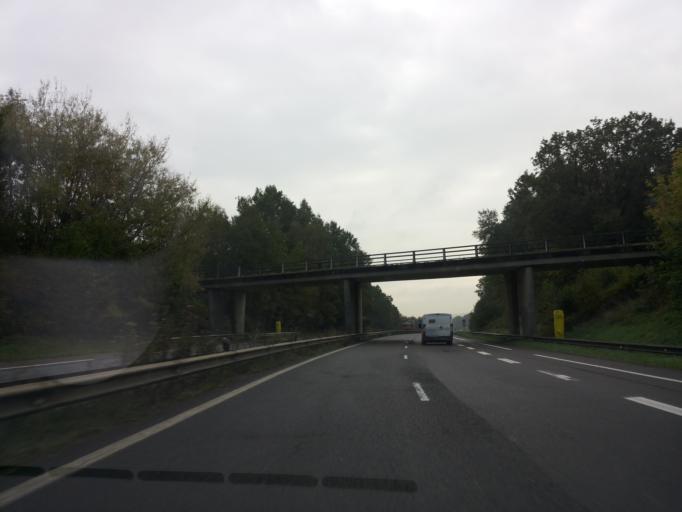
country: FR
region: Champagne-Ardenne
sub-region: Departement des Ardennes
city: Bazeilles
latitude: 49.6847
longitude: 4.9894
